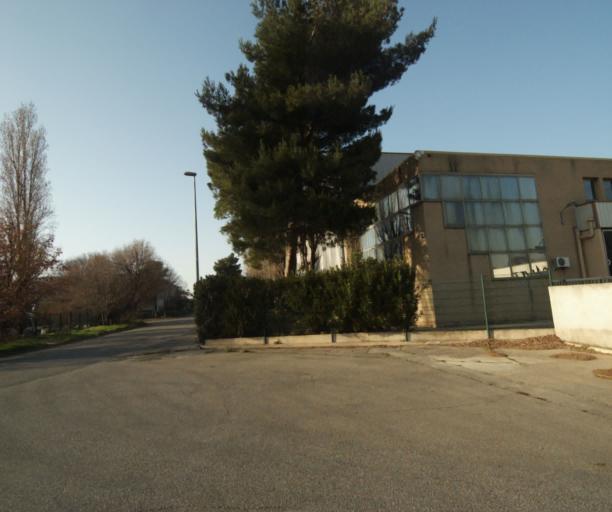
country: FR
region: Provence-Alpes-Cote d'Azur
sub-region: Departement des Bouches-du-Rhone
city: Saint-Victoret
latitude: 43.4176
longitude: 5.2717
